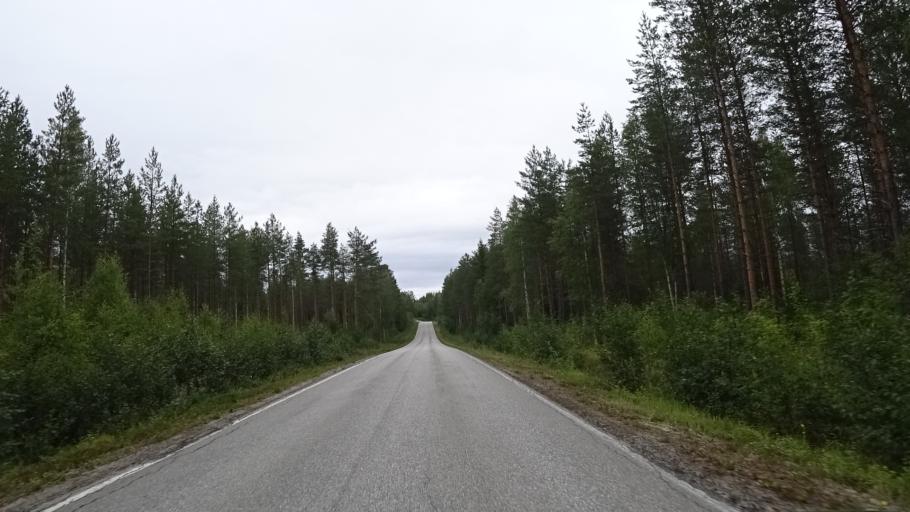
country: FI
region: North Karelia
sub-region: Pielisen Karjala
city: Lieksa
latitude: 63.3714
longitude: 30.2985
